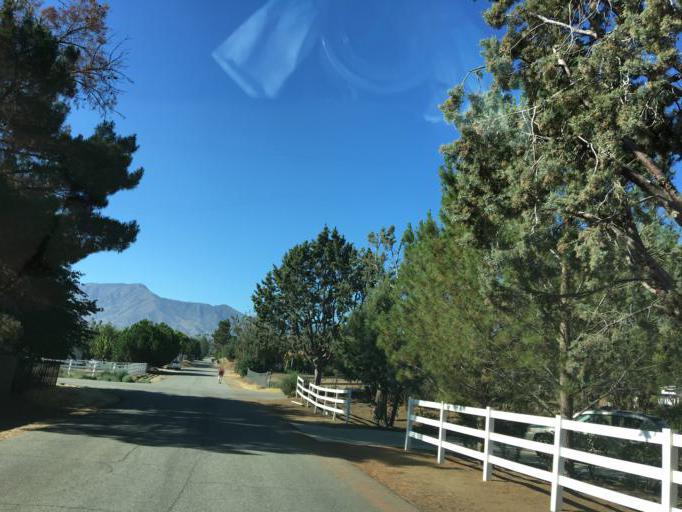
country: US
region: California
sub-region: Los Angeles County
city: Acton
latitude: 34.4713
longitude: -118.1998
